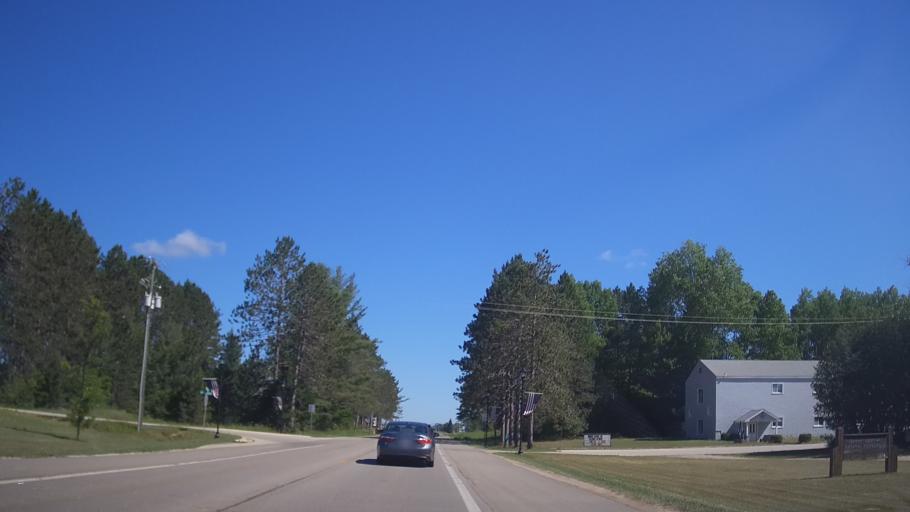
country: US
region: Michigan
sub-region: Cheboygan County
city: Indian River
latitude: 45.5551
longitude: -84.7844
